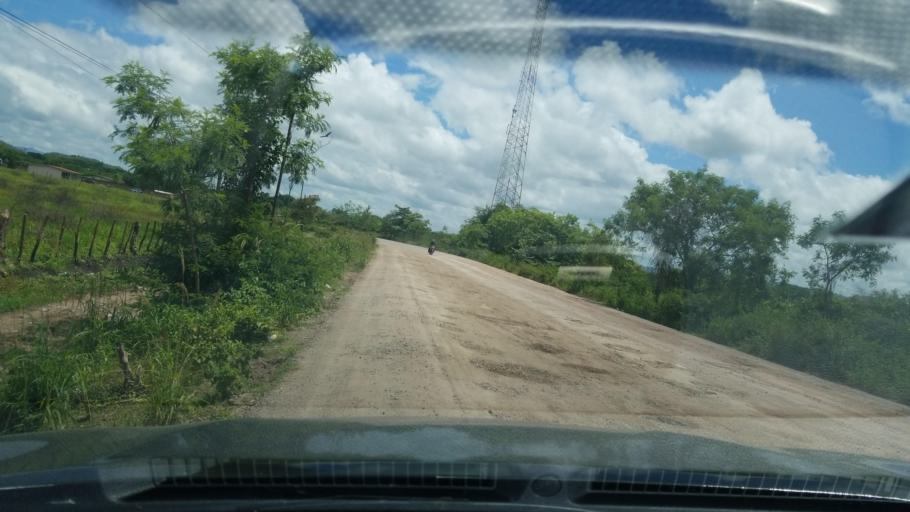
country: HN
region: Francisco Morazan
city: Talanga
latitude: 14.3652
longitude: -87.0527
